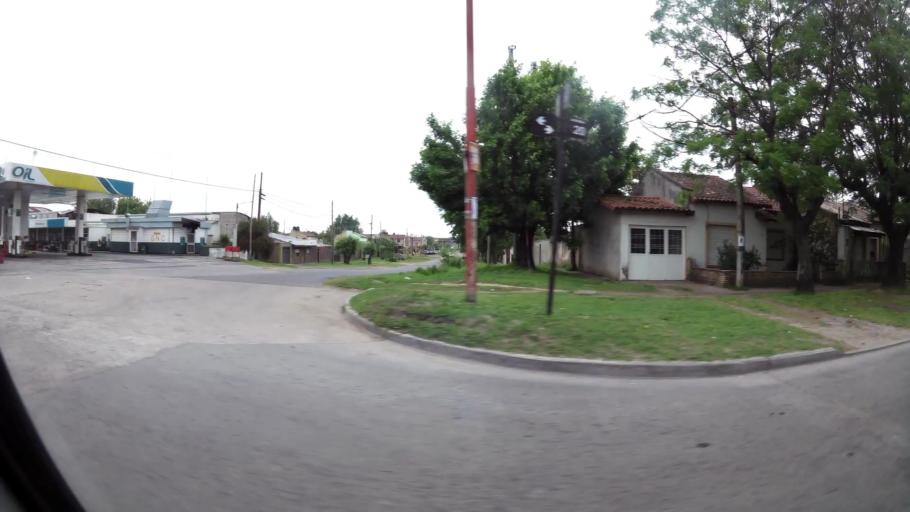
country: AR
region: Buenos Aires
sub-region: Partido de La Plata
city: La Plata
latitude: -34.8842
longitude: -57.9633
